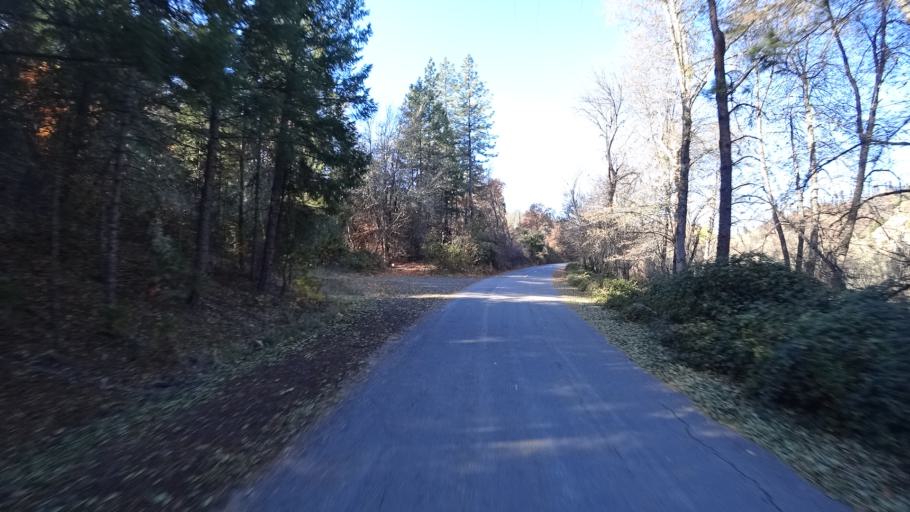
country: US
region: California
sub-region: Siskiyou County
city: Yreka
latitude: 41.8221
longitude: -122.9630
